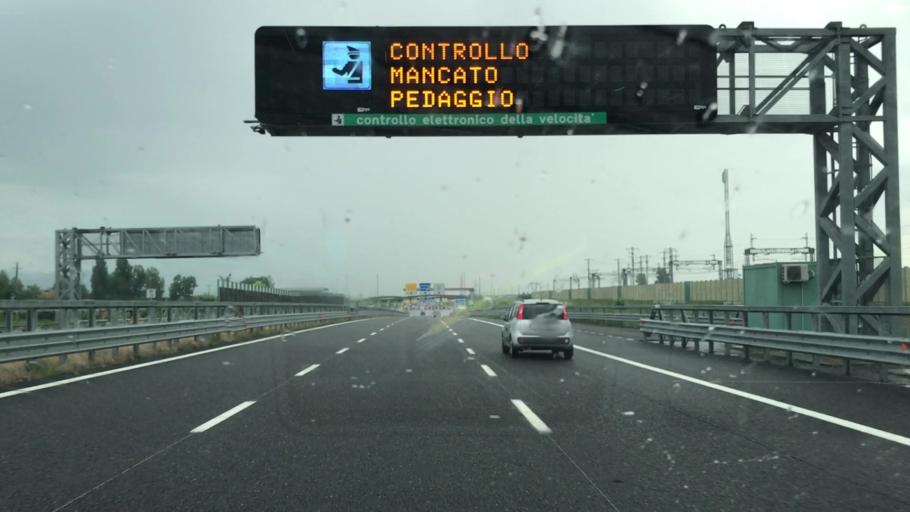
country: IT
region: Lombardy
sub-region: Provincia di Brescia
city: Castelcovati
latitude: 45.5211
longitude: 9.9534
